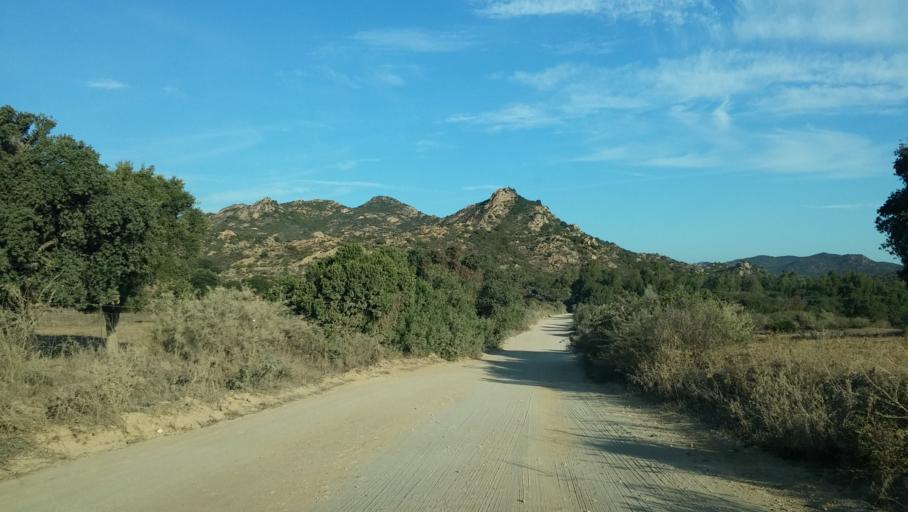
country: IT
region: Sardinia
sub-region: Provincia di Nuoro
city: La Caletta
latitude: 40.4822
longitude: 9.8043
